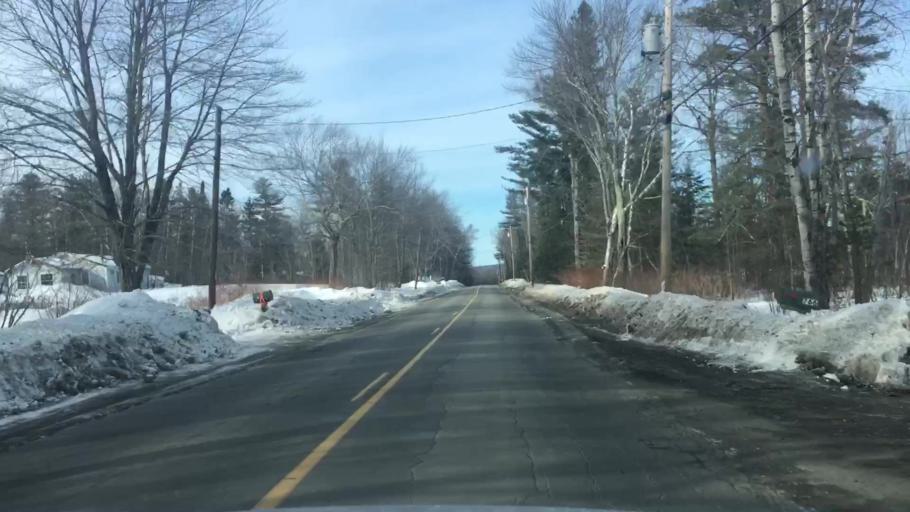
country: US
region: Maine
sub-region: Penobscot County
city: Charleston
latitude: 45.0349
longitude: -69.0323
